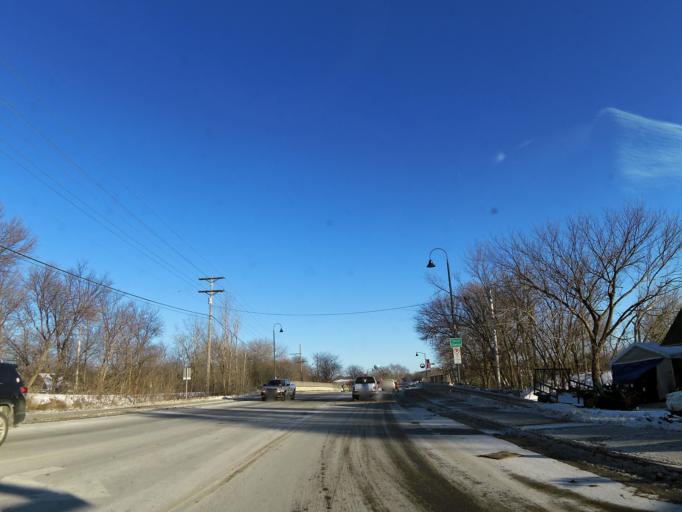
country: US
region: Minnesota
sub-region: Hennepin County
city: Spring Park
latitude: 44.9370
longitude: -93.6459
